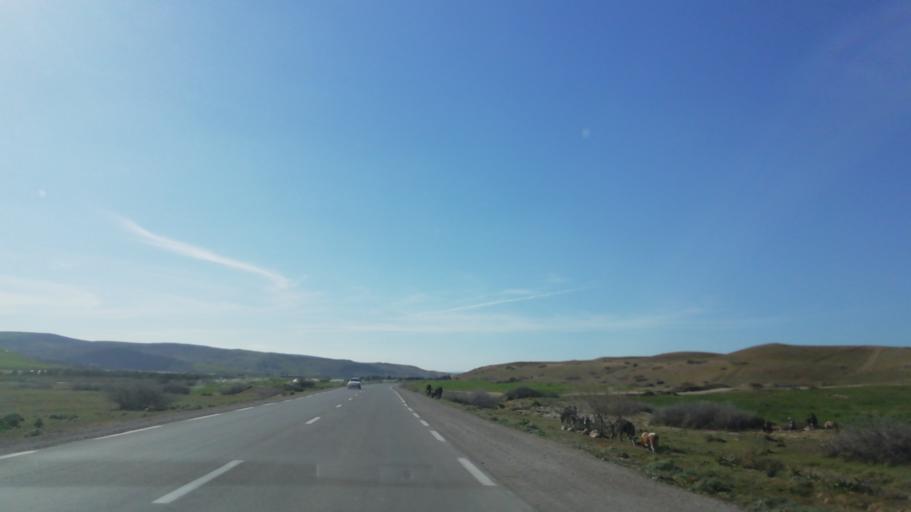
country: DZ
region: Mascara
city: Oued el Abtal
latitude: 35.4497
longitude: 0.7952
